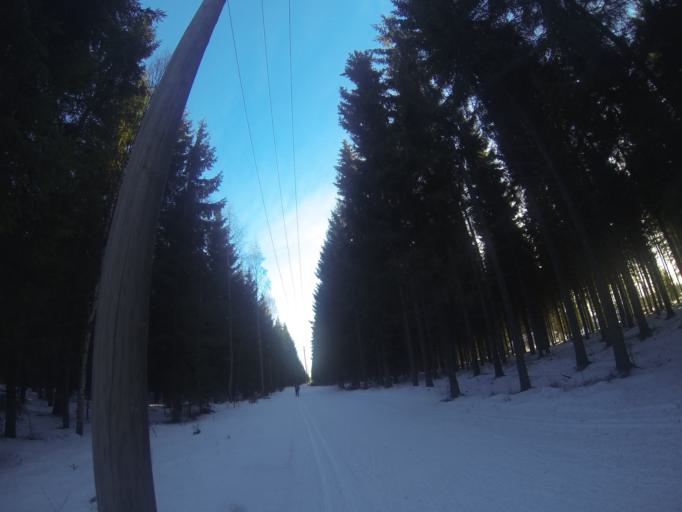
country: FI
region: Southern Savonia
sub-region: Savonlinna
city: Savonlinna
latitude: 61.9268
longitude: 28.8946
